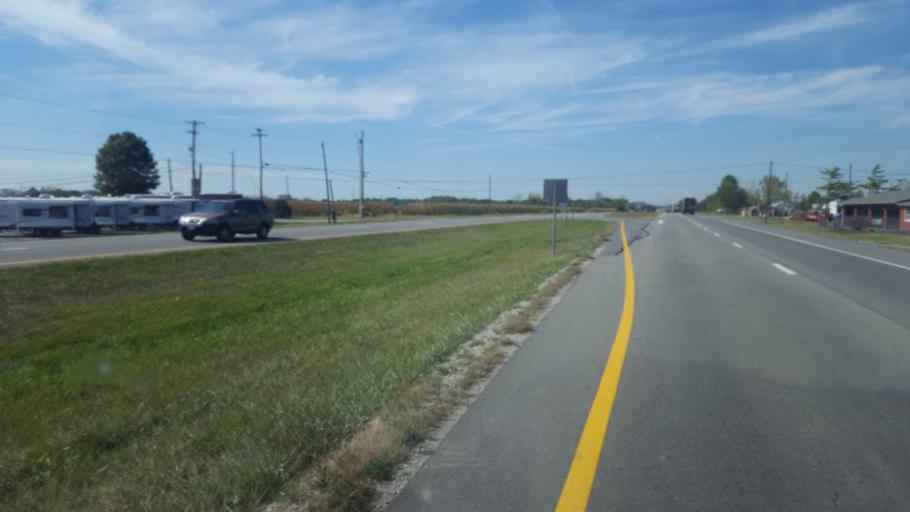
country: US
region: Ohio
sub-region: Delaware County
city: Lewis Center
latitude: 40.2724
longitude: -82.9625
